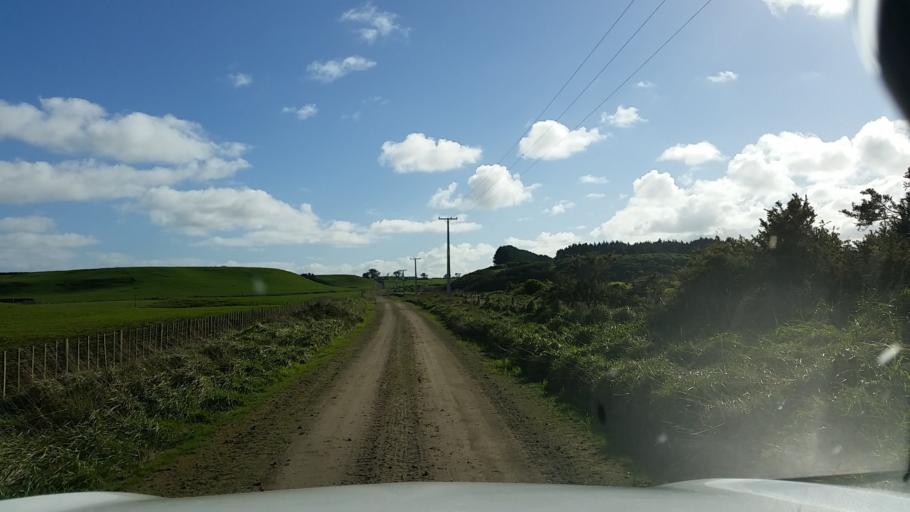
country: NZ
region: Taranaki
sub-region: South Taranaki District
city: Patea
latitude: -39.7195
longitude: 174.4702
